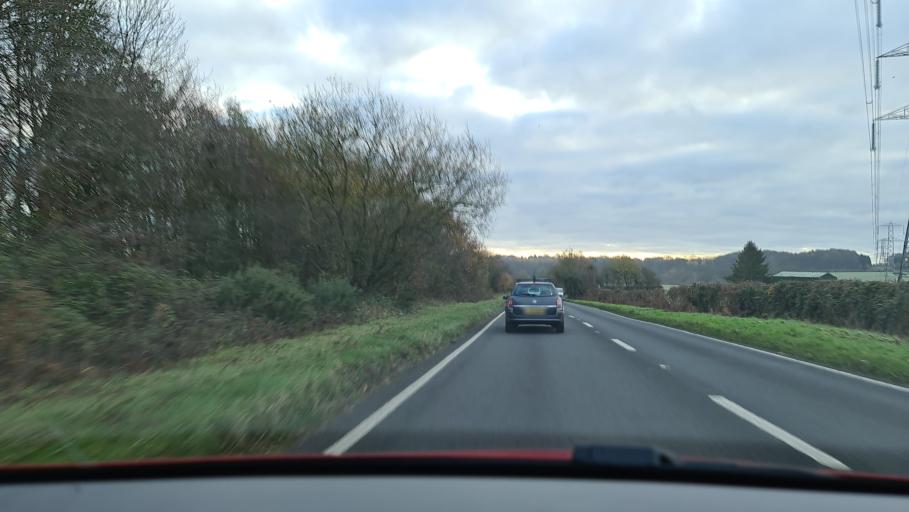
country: GB
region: England
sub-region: Buckinghamshire
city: Amersham
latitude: 51.6556
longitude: -0.6525
